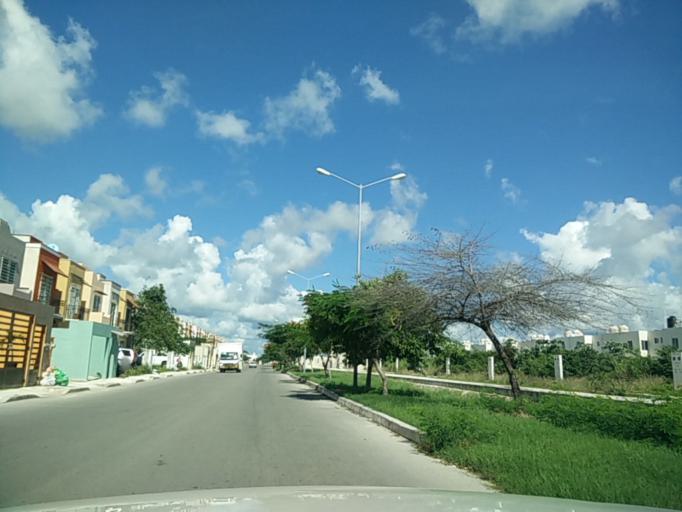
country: MX
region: Quintana Roo
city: Playa del Carmen
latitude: 20.6624
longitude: -87.0636
